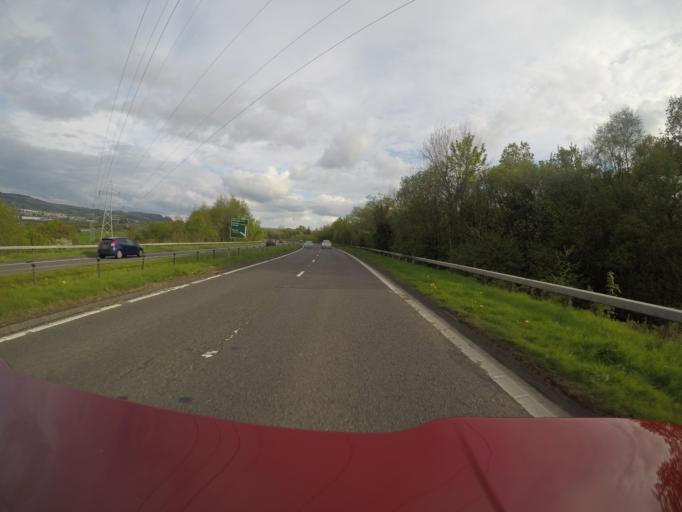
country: GB
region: Scotland
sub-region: West Dunbartonshire
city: Renton
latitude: 55.9644
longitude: -4.5872
